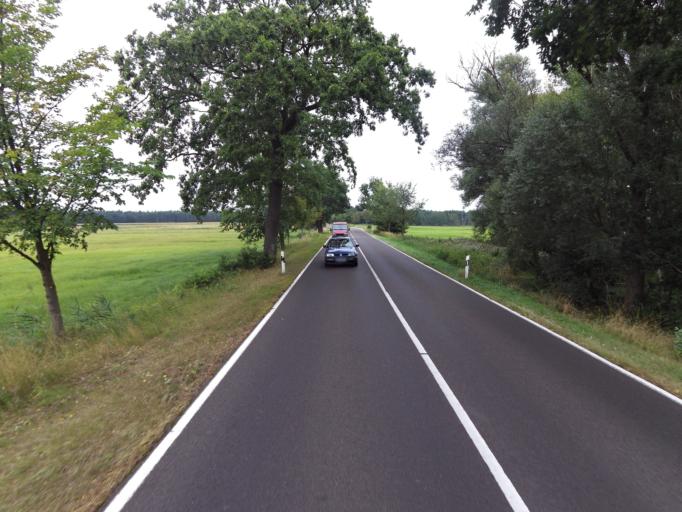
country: DE
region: Brandenburg
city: Liebenwalde
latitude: 52.9236
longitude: 13.3868
